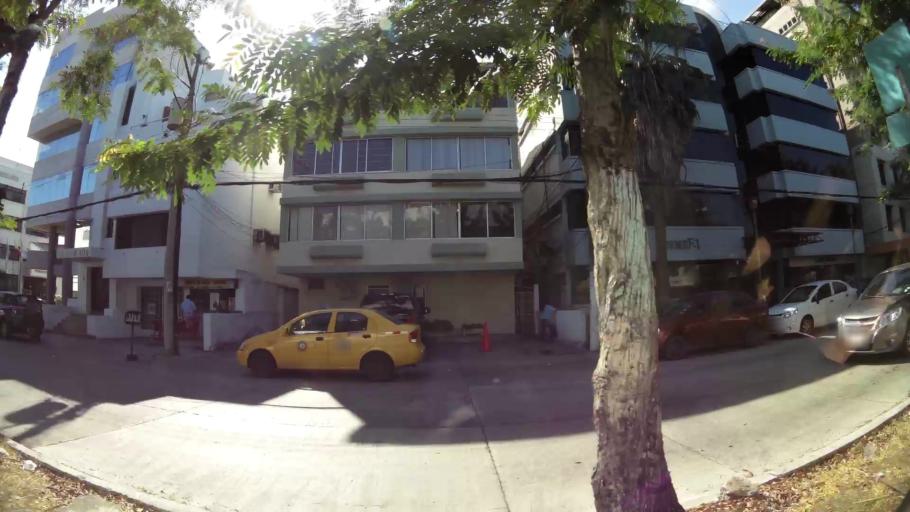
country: EC
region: Guayas
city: Guayaquil
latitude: -2.1607
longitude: -79.8998
